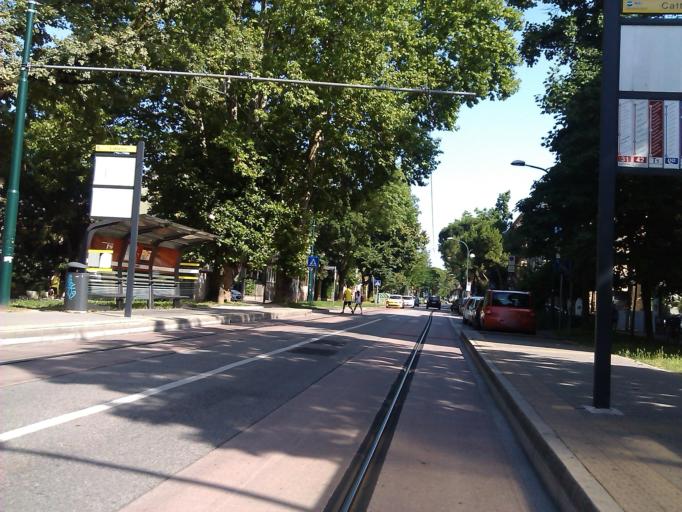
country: IT
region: Veneto
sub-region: Provincia di Venezia
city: Mestre
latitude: 45.4902
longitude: 12.2513
